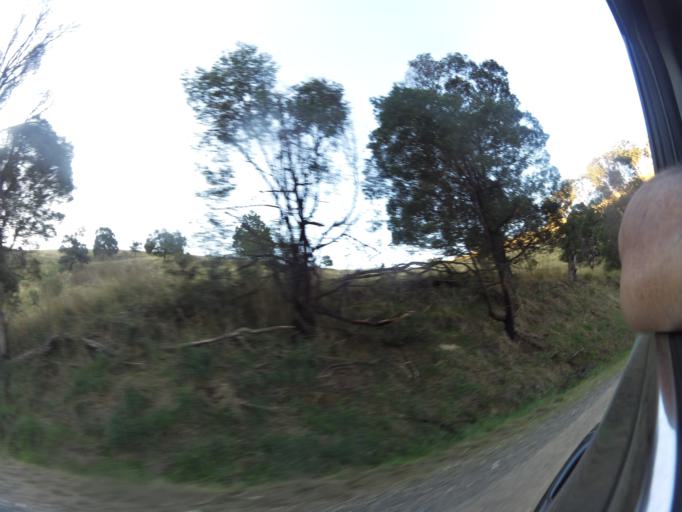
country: AU
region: Victoria
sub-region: Murrindindi
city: Alexandra
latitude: -37.1468
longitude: 145.5216
